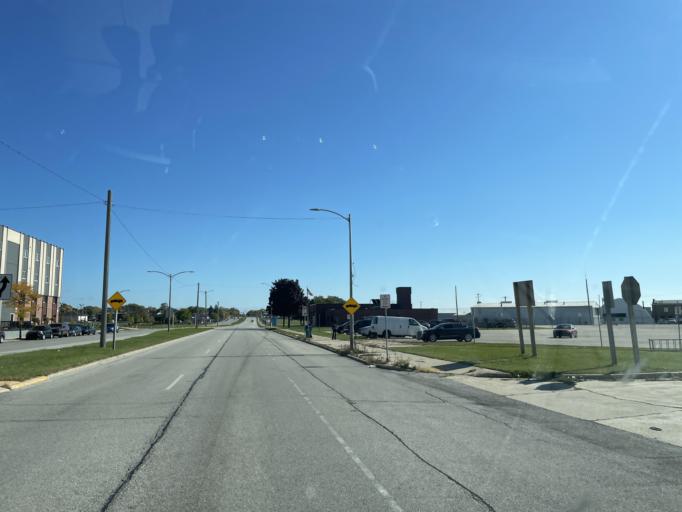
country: US
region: Wisconsin
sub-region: Waukesha County
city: Butler
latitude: 43.1176
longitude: -88.0324
